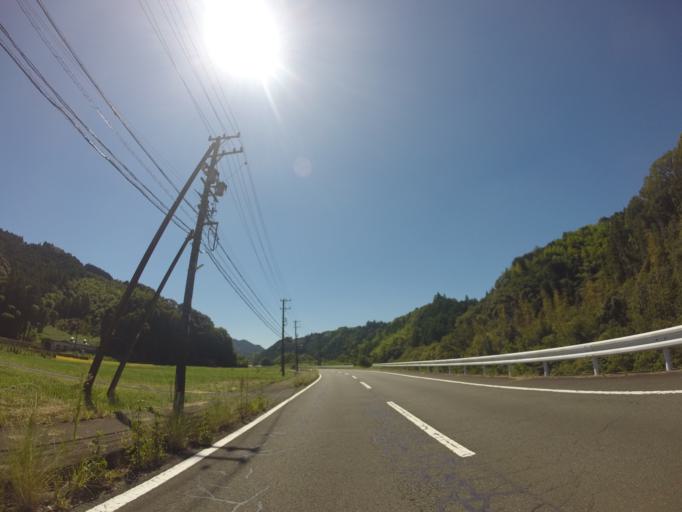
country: JP
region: Shizuoka
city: Fujieda
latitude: 34.9328
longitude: 138.2040
